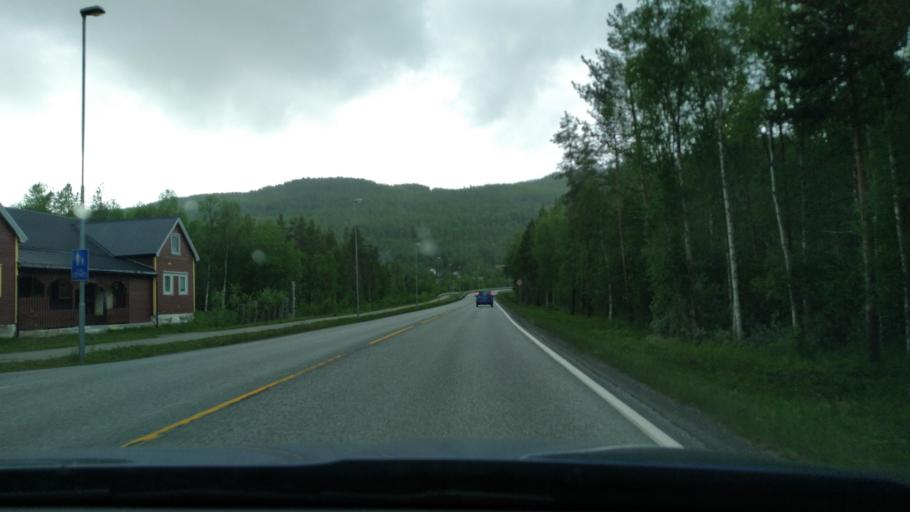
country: NO
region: Troms
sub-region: Malselv
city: Moen
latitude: 69.0096
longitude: 18.4950
